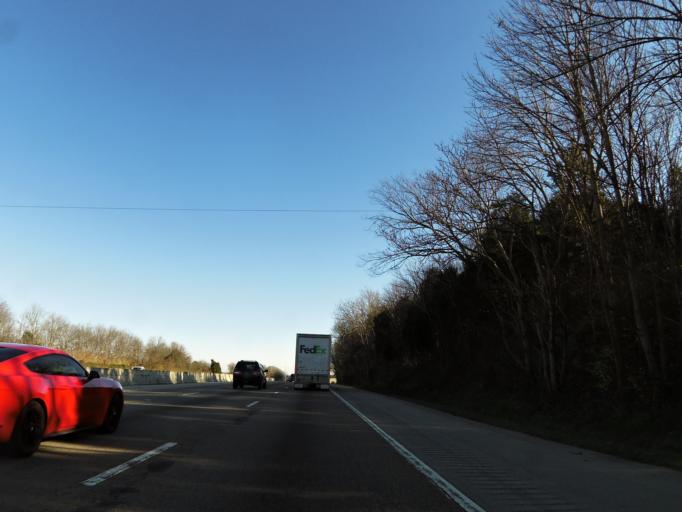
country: US
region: Tennessee
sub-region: Jefferson County
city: Dandridge
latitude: 36.0648
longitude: -83.3929
